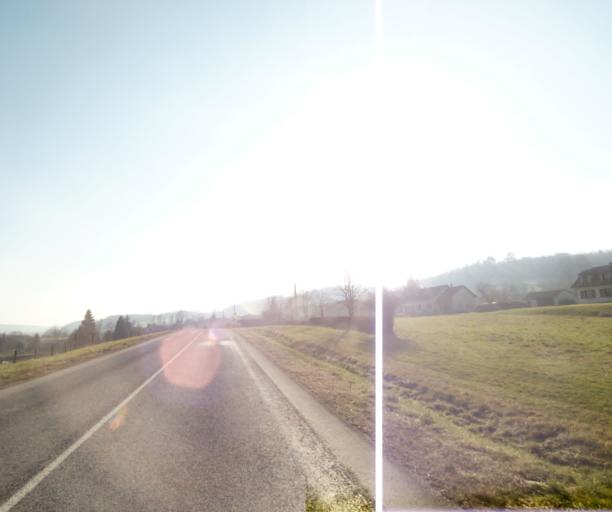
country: FR
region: Champagne-Ardenne
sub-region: Departement de la Haute-Marne
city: Chevillon
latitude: 48.5088
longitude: 5.1129
